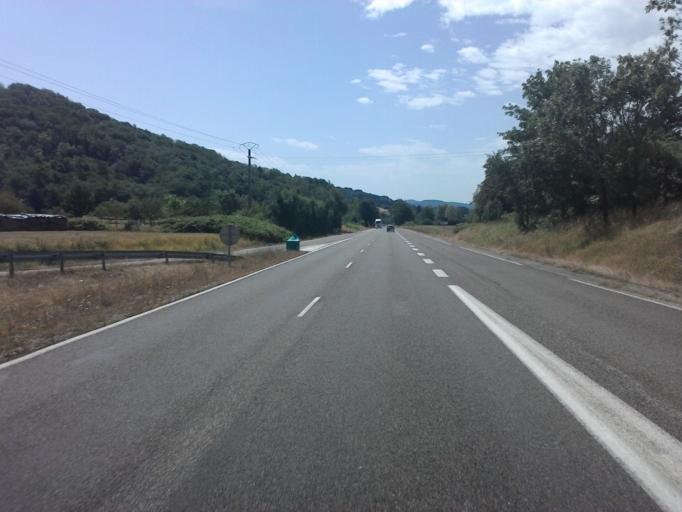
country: FR
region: Franche-Comte
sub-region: Departement du Jura
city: Cousance
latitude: 46.5379
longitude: 5.3971
